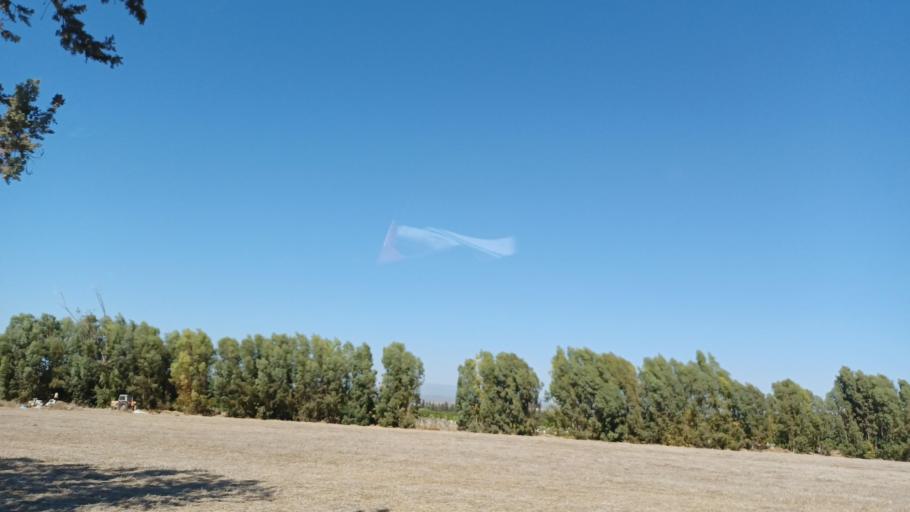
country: CY
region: Larnaka
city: Kolossi
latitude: 34.6333
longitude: 32.9318
